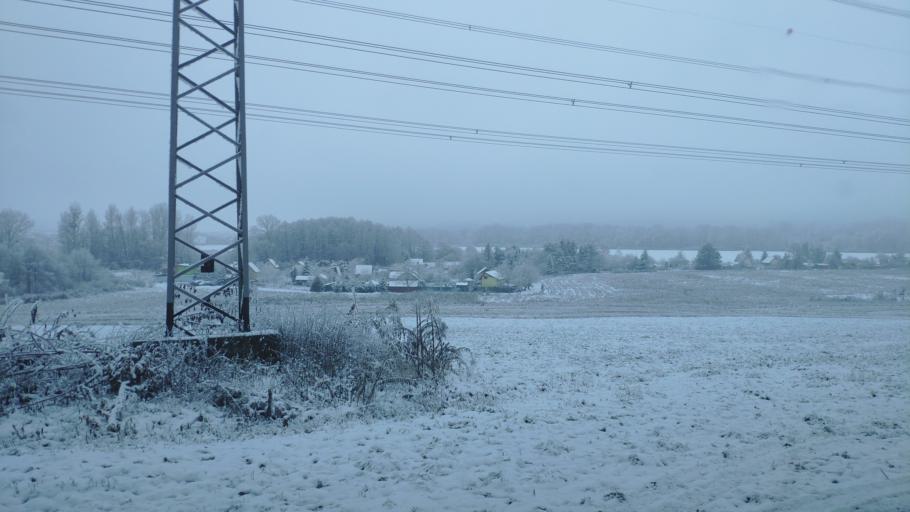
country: SK
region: Kosicky
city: Kosice
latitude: 48.6452
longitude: 21.1739
